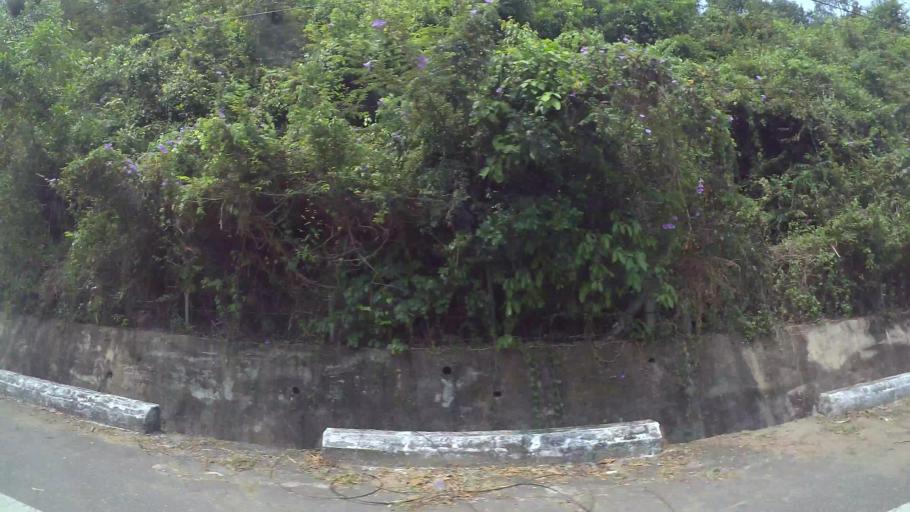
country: VN
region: Da Nang
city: Son Tra
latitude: 16.1066
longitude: 108.2921
